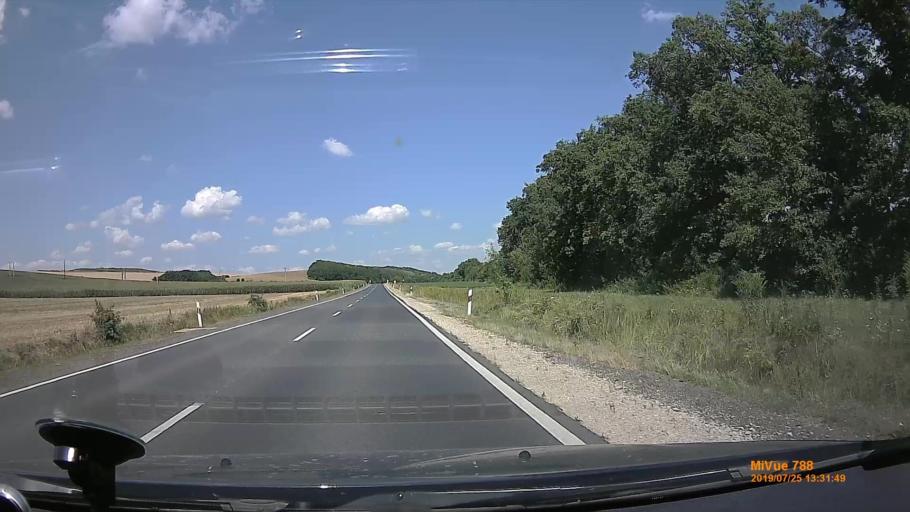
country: HU
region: Borsod-Abauj-Zemplen
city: Encs
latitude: 48.3684
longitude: 21.1417
